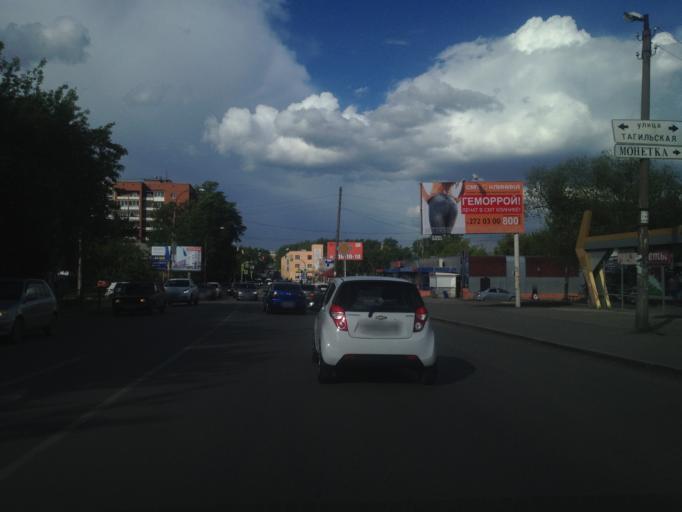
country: RU
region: Sverdlovsk
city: Yekaterinburg
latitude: 56.8633
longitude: 60.5755
